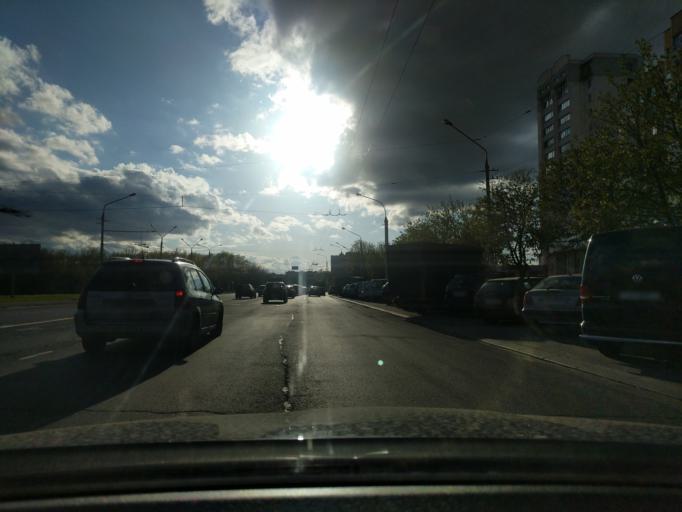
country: BY
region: Minsk
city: Novoye Medvezhino
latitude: 53.8938
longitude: 27.4835
